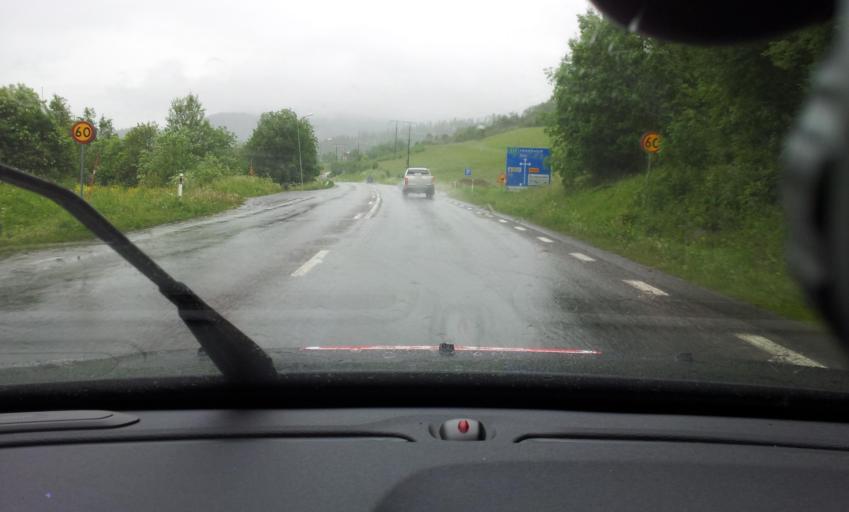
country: SE
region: Jaemtland
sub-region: Are Kommun
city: Are
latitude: 63.3763
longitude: 13.1580
